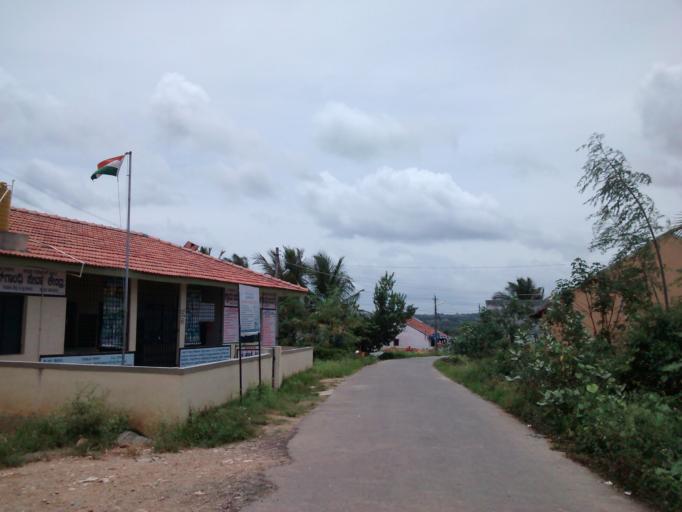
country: IN
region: Karnataka
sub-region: Hassan
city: Hassan
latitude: 12.9245
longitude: 76.1331
